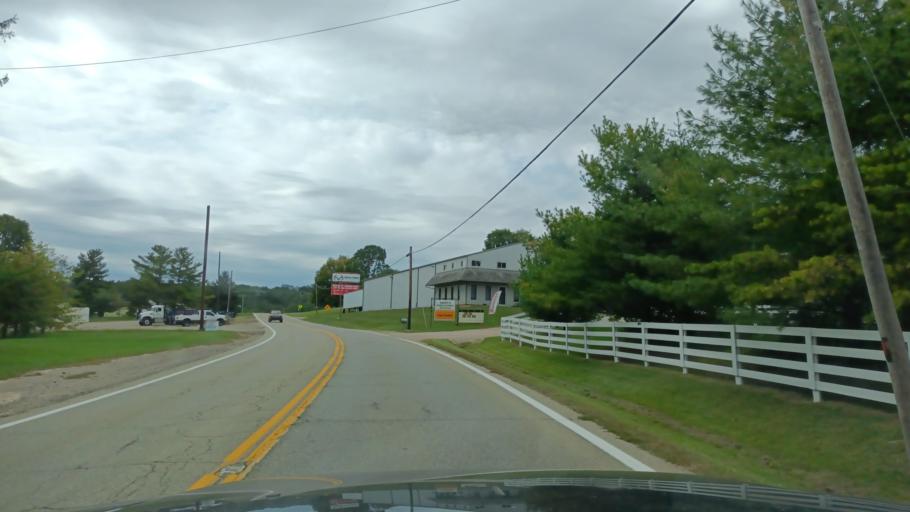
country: US
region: Ohio
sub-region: Vinton County
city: McArthur
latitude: 39.2626
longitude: -82.5080
